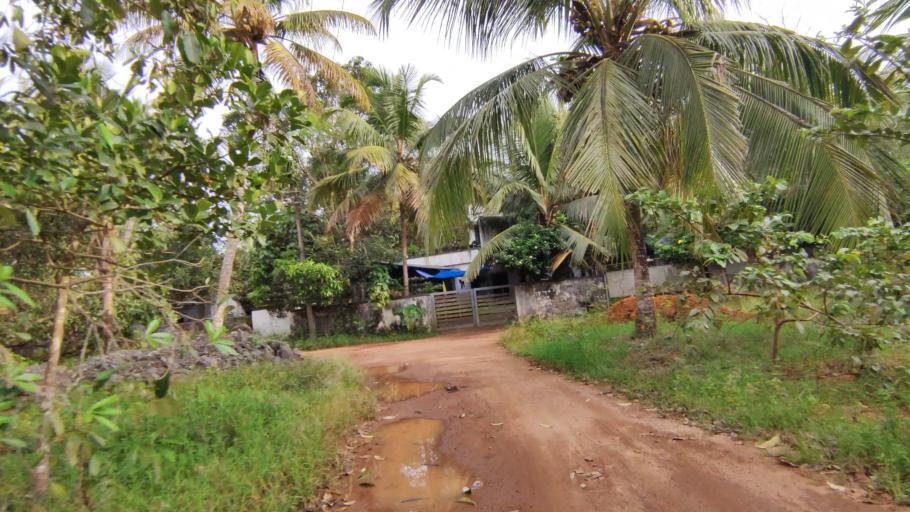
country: IN
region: Kerala
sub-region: Alappuzha
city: Shertallai
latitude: 9.6211
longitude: 76.3343
